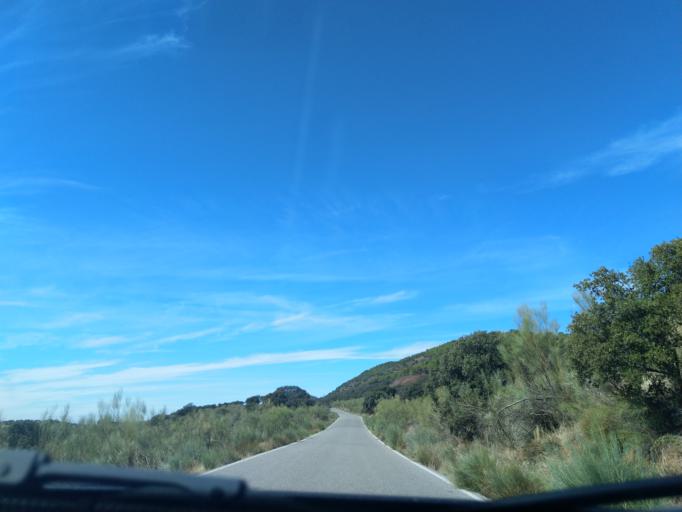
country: ES
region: Extremadura
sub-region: Provincia de Badajoz
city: Reina
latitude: 38.1159
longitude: -5.9252
